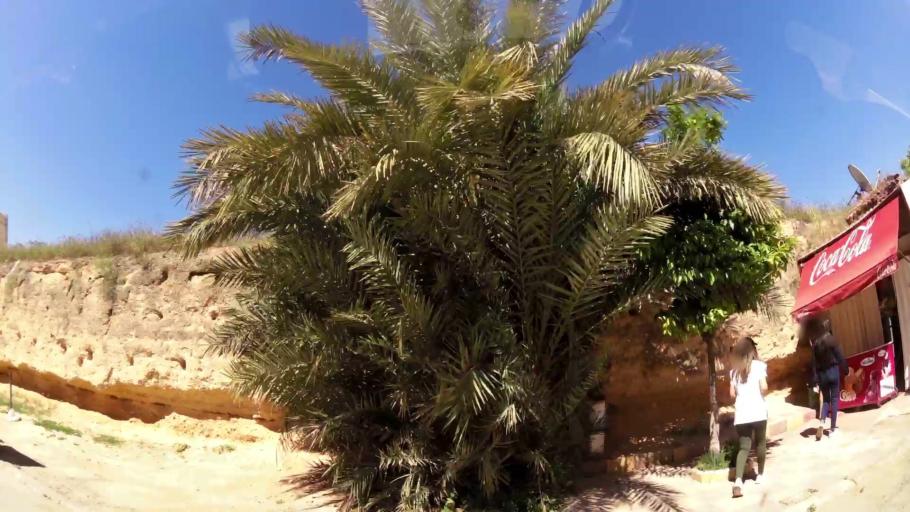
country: MA
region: Meknes-Tafilalet
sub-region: Meknes
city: Meknes
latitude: 33.8820
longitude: -5.5618
